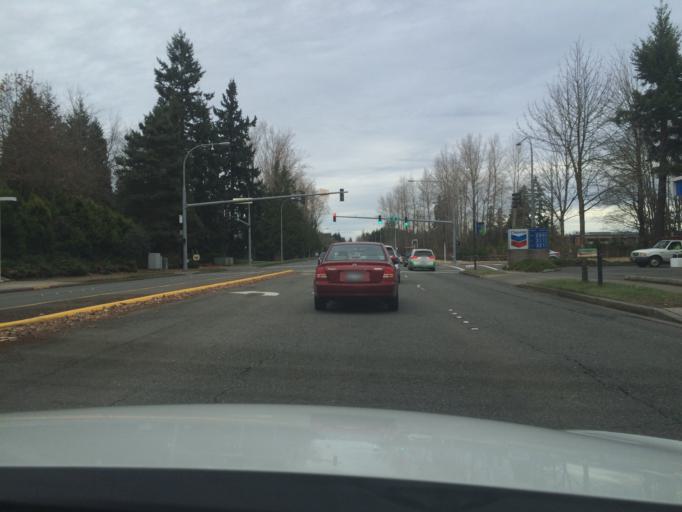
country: US
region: Washington
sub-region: King County
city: Redmond
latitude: 47.6545
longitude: -122.1432
